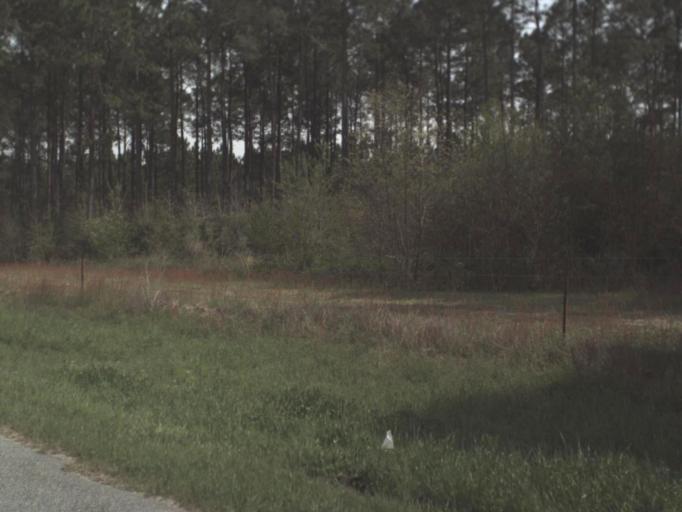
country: US
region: Florida
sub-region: Jackson County
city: Malone
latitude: 30.9756
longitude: -85.0666
